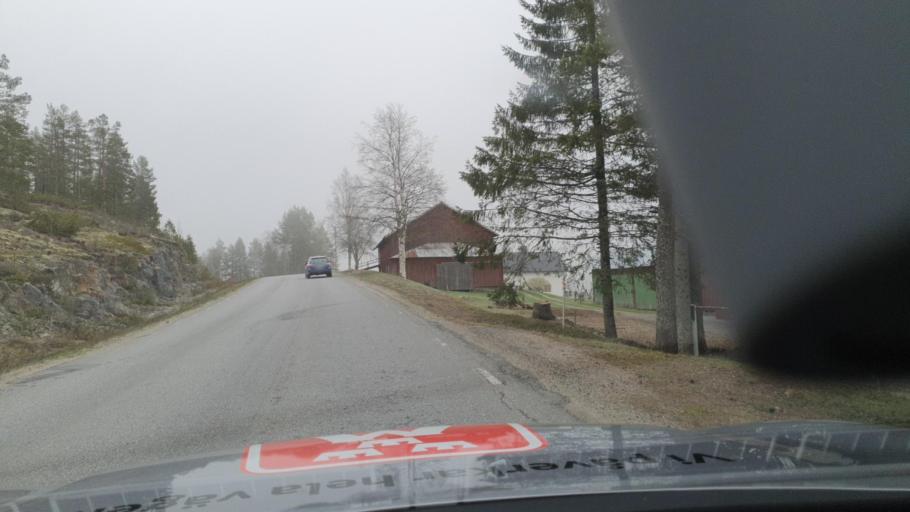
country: SE
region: Vaesternorrland
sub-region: OErnskoeldsviks Kommun
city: Husum
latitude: 63.4894
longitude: 19.1784
